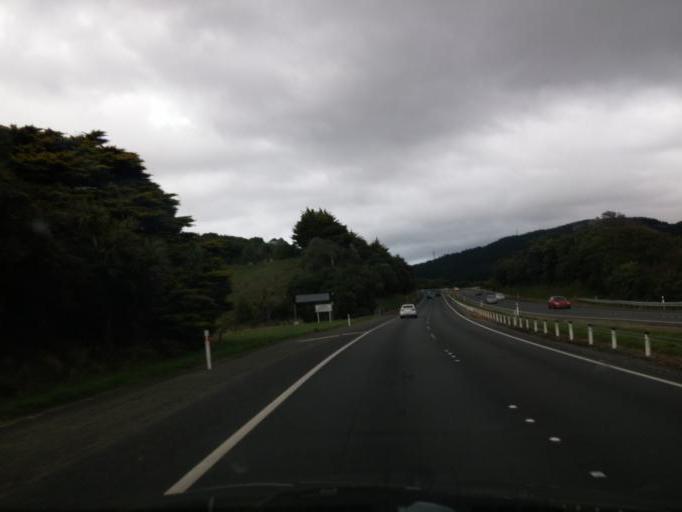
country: NZ
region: Wellington
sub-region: Porirua City
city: Porirua
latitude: -41.1768
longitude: 174.8301
